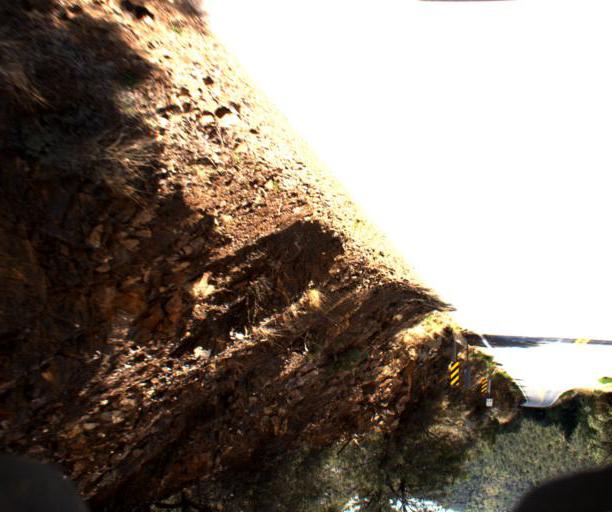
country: US
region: Arizona
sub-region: Yavapai County
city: Clarkdale
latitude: 34.6841
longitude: -112.1702
